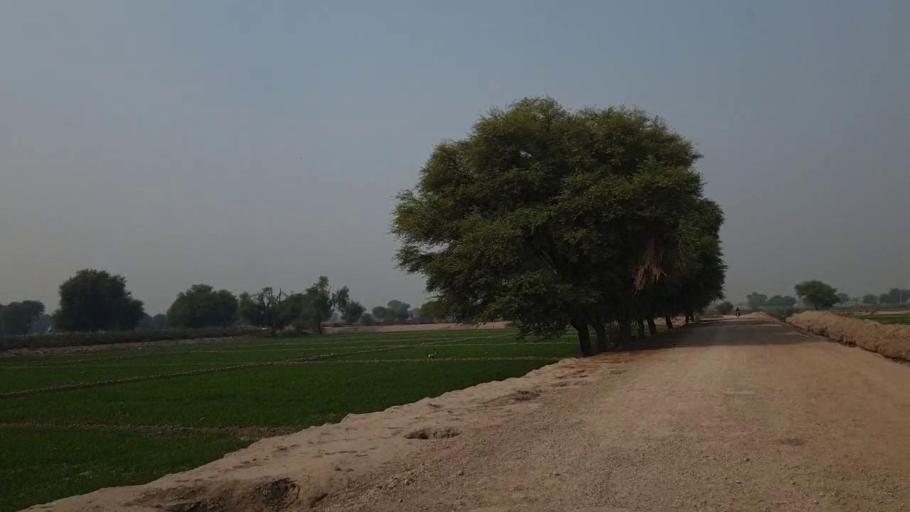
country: PK
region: Sindh
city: Bhan
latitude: 26.5300
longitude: 67.7141
